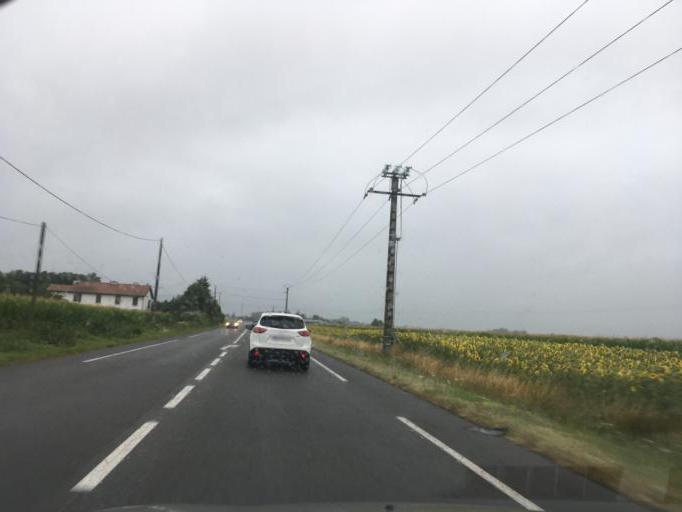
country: FR
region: Midi-Pyrenees
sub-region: Departement des Hautes-Pyrenees
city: Bazet
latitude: 43.2998
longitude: 0.0681
